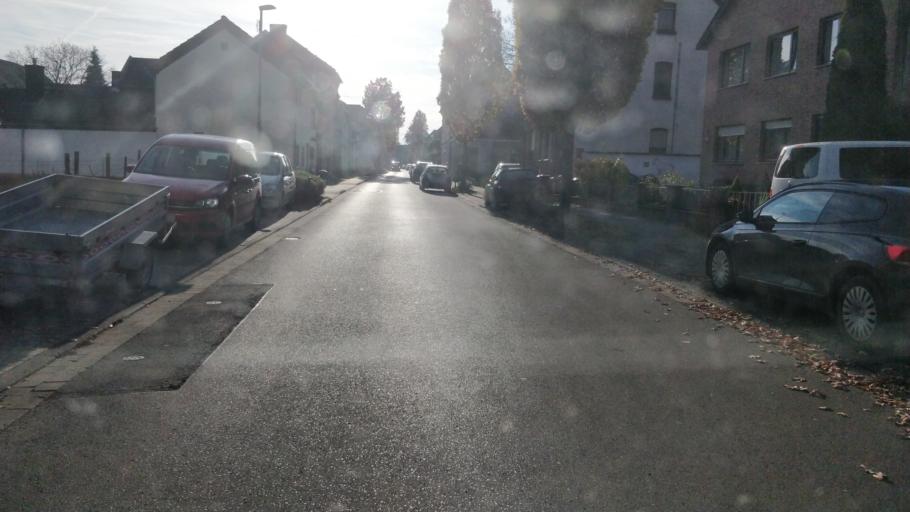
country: DE
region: North Rhine-Westphalia
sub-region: Regierungsbezirk Koln
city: Euskirchen
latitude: 50.6273
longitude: 6.8522
